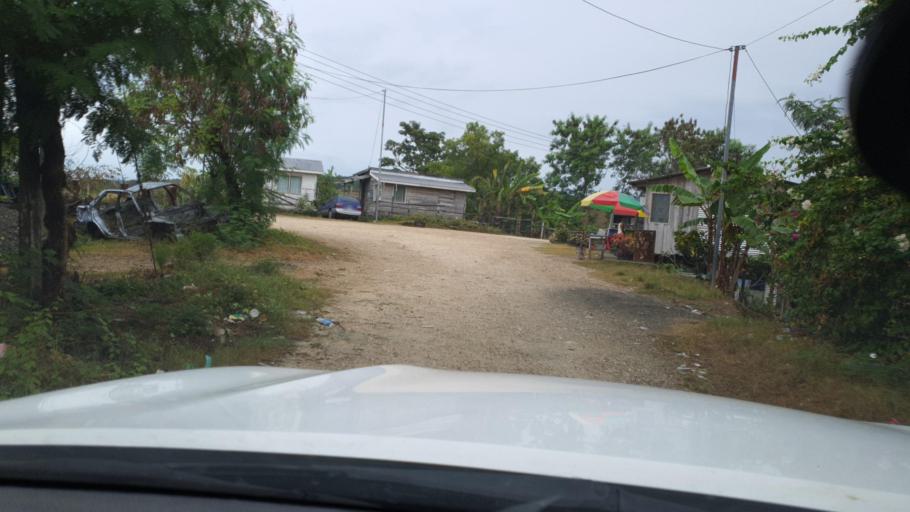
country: SB
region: Guadalcanal
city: Honiara
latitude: -9.4433
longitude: 159.9638
